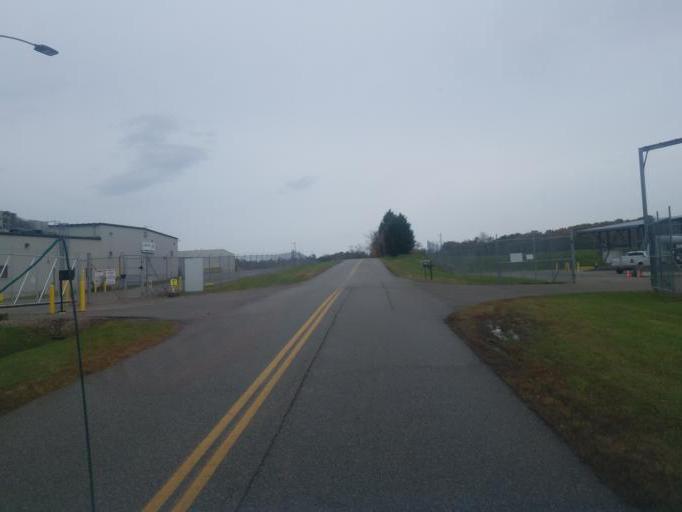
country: US
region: Ohio
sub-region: Washington County
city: Beverly
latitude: 39.5340
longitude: -81.7159
